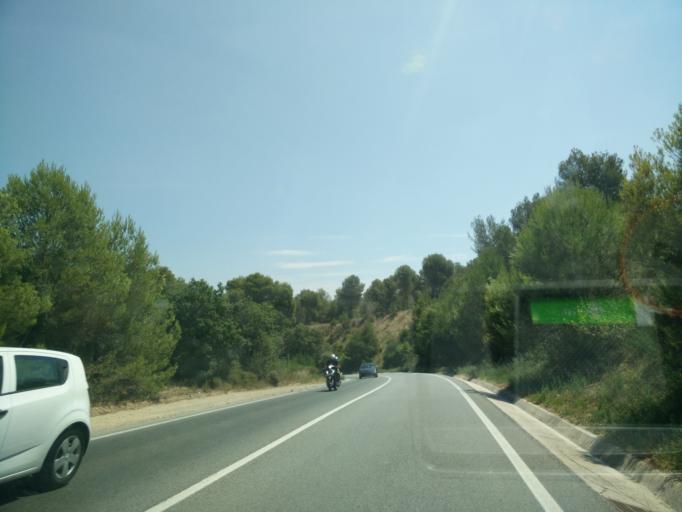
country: ES
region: Catalonia
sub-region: Provincia de Barcelona
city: Esparreguera
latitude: 41.5195
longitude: 1.8602
